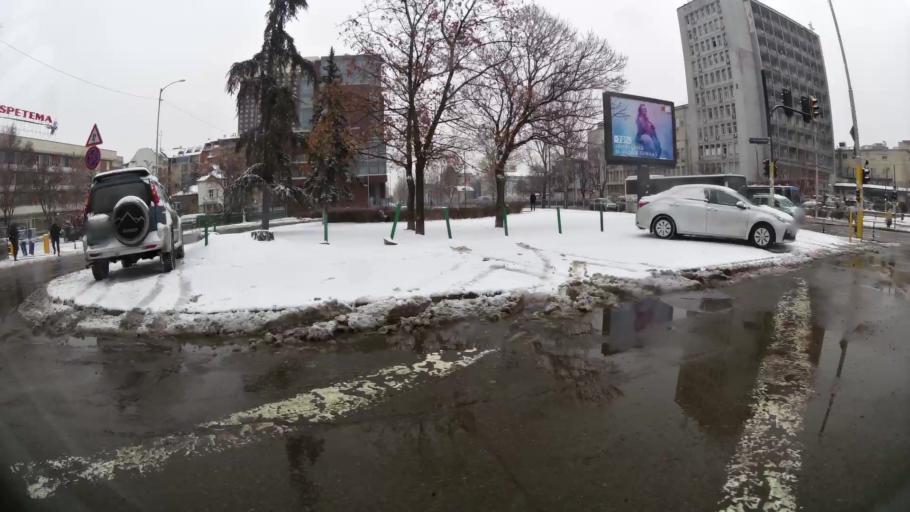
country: BG
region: Sofia-Capital
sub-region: Stolichna Obshtina
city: Sofia
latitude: 42.6904
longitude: 23.3063
